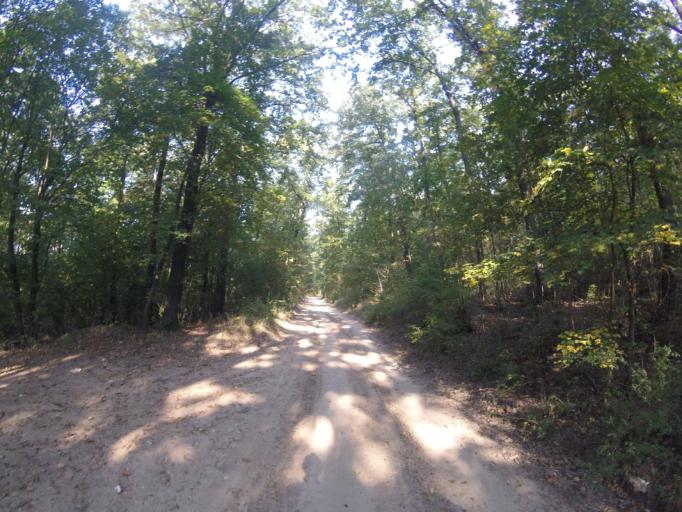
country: HU
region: Komarom-Esztergom
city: Piliscsev
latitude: 47.6895
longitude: 18.8504
